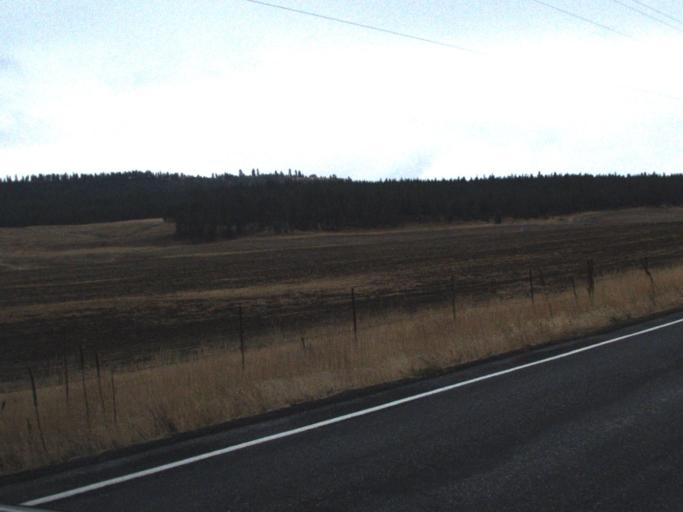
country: US
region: Washington
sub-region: Spokane County
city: Fairchild Air Force Base
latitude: 47.8215
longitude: -117.8837
